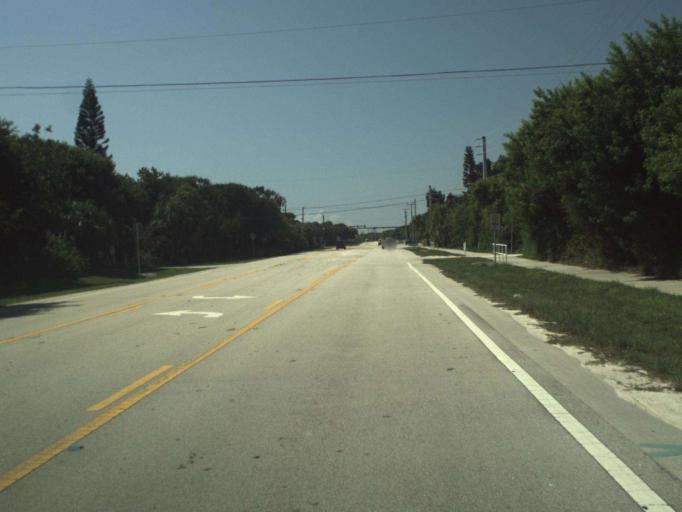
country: US
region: Florida
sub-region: Indian River County
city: Wabasso Beach
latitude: 27.7661
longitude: -80.3999
